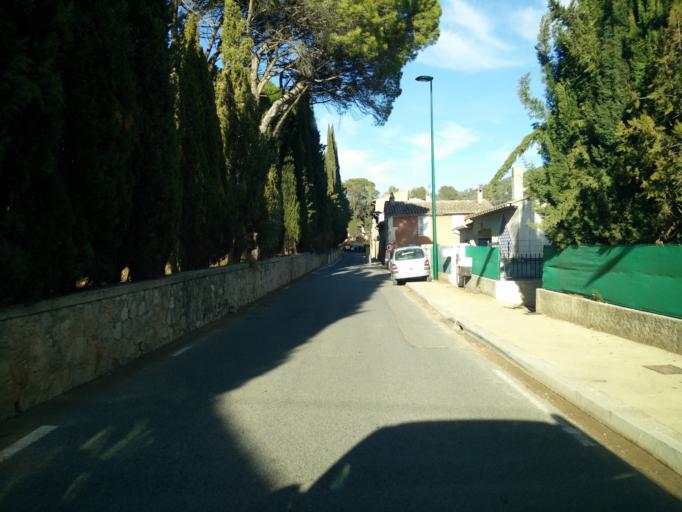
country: FR
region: Provence-Alpes-Cote d'Azur
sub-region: Departement du Var
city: Taradeau
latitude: 43.4526
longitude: 6.4238
